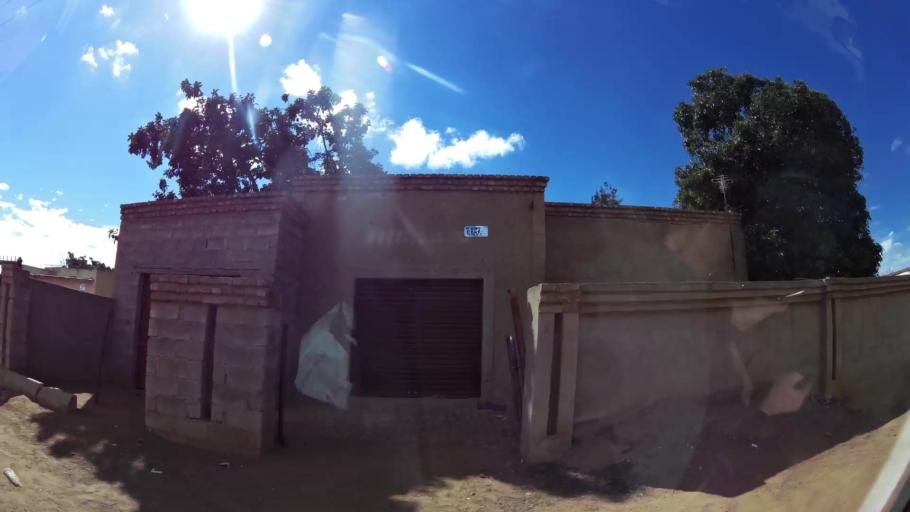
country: ZA
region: Limpopo
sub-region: Waterberg District Municipality
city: Bela-Bela
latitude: -24.8792
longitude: 28.3271
